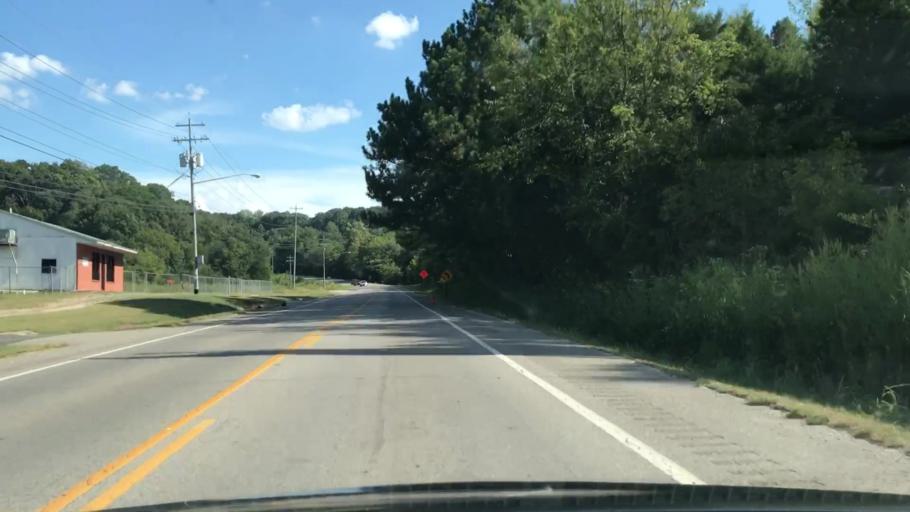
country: US
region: Alabama
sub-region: Limestone County
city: Ardmore
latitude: 35.0088
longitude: -86.8759
